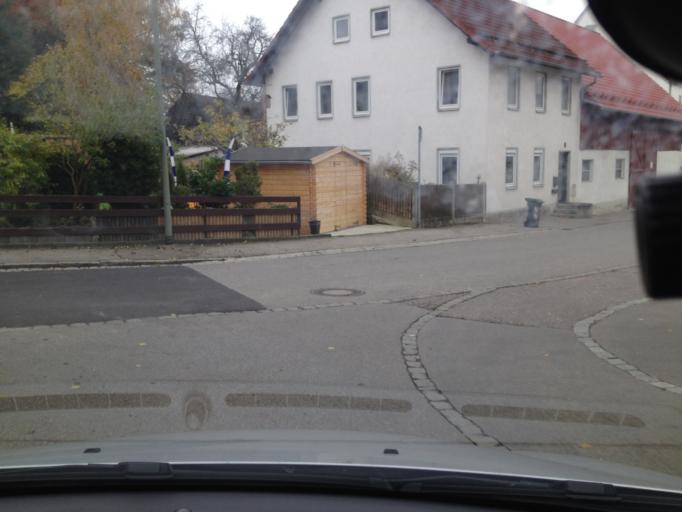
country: DE
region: Bavaria
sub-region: Swabia
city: Schwabmunchen
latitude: 48.1830
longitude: 10.7573
